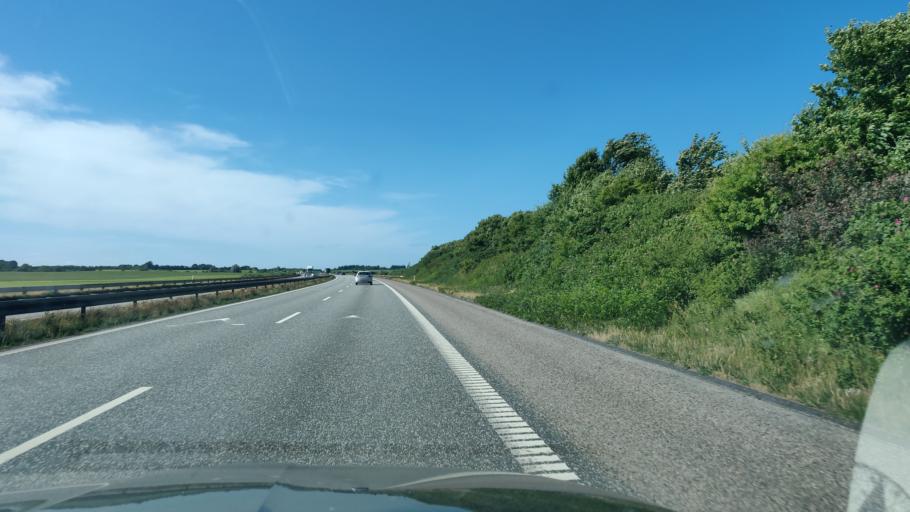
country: DK
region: North Denmark
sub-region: Mariagerfjord Kommune
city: Hobro
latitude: 56.7144
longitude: 9.7260
